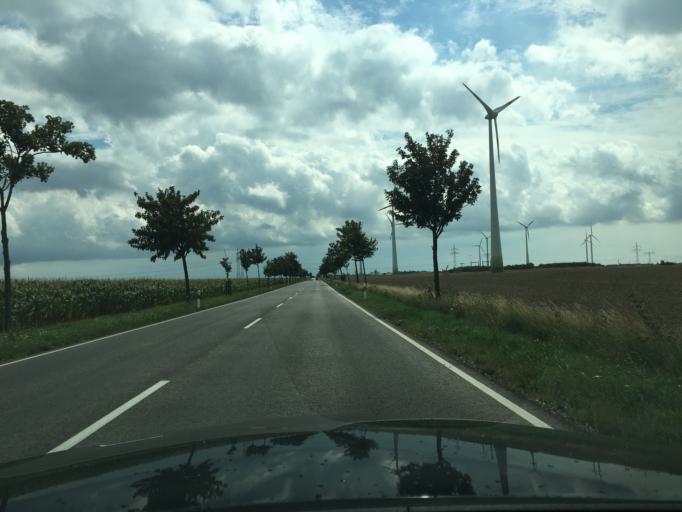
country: DE
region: Saxony-Anhalt
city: Raguhn
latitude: 51.7182
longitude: 12.2422
